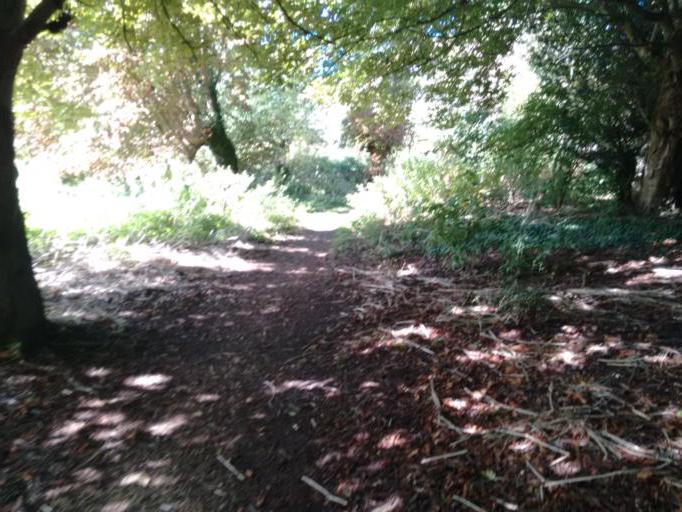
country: GB
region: England
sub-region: Oxfordshire
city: Eynsham
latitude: 51.7782
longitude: -1.3744
